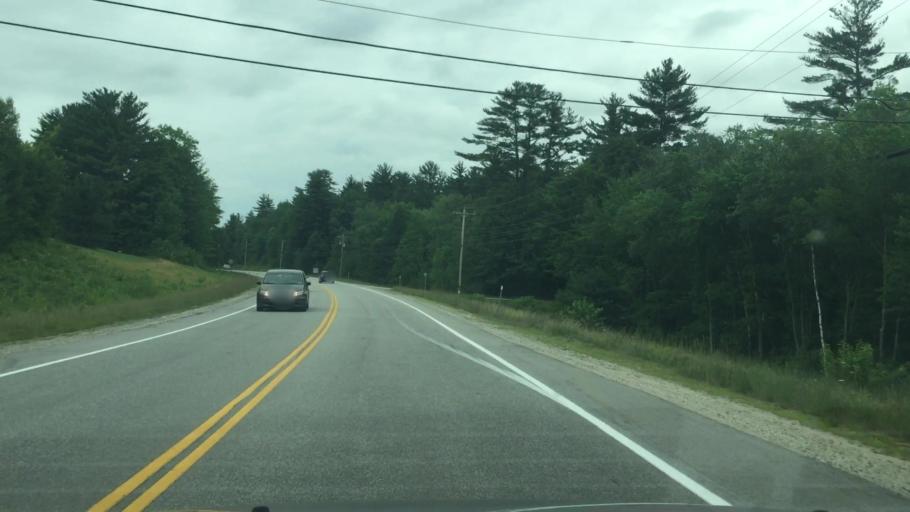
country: US
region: New Hampshire
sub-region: Carroll County
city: Moultonborough
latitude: 43.7699
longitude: -71.3827
